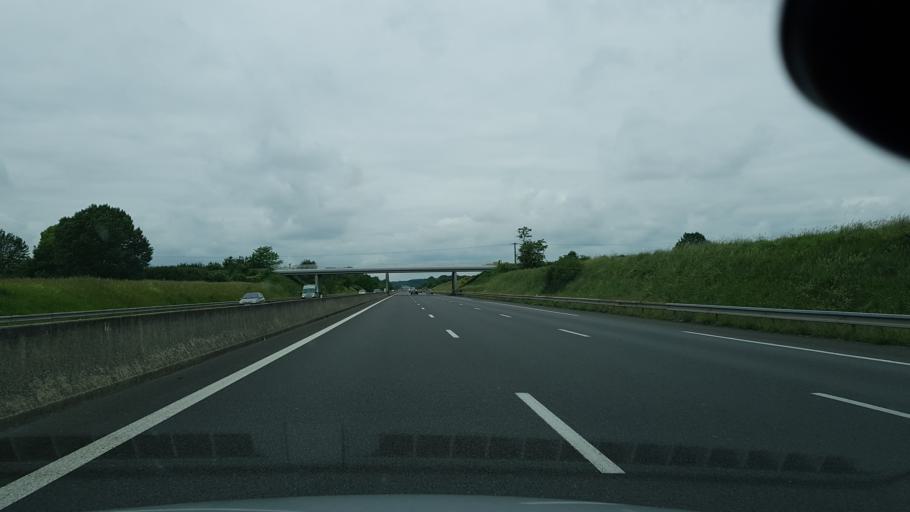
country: FR
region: Centre
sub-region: Departement du Loir-et-Cher
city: Saint-Sulpice-de-Pommeray
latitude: 47.6165
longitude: 1.2850
